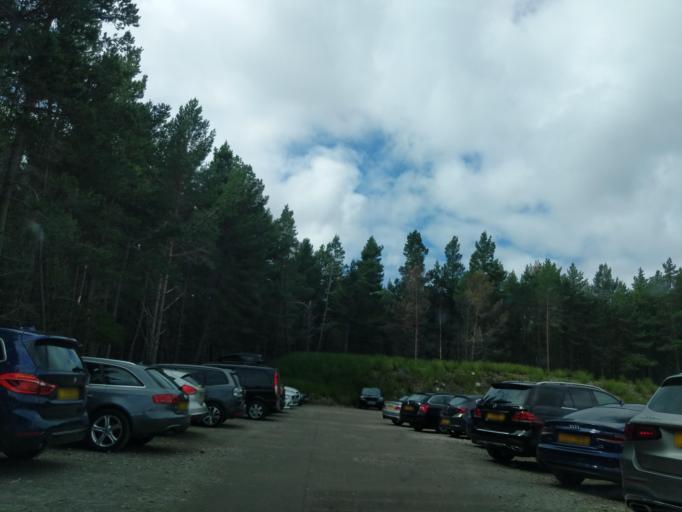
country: GB
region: Scotland
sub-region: Highland
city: Aviemore
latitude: 57.2786
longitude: -3.8181
